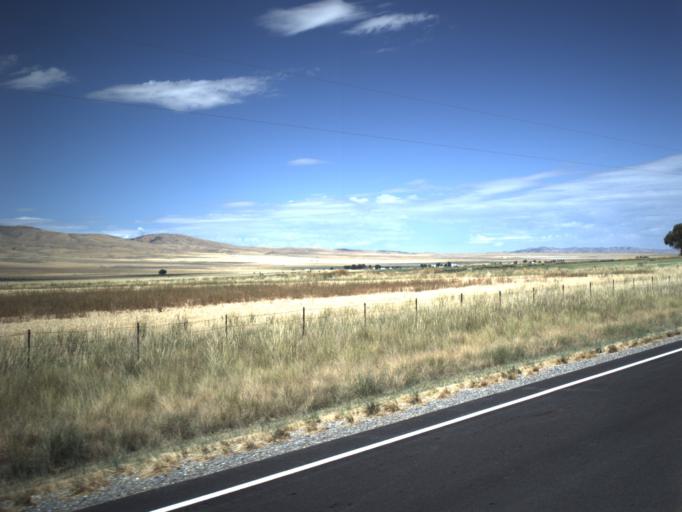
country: US
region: Utah
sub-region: Box Elder County
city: Garland
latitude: 41.7727
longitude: -112.4351
